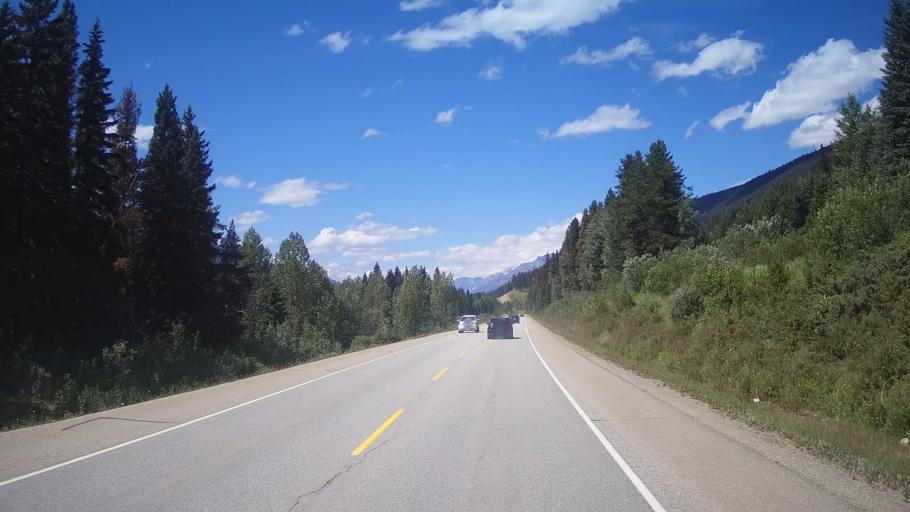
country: CA
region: Alberta
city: Jasper Park Lodge
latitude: 52.8742
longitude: -118.6887
